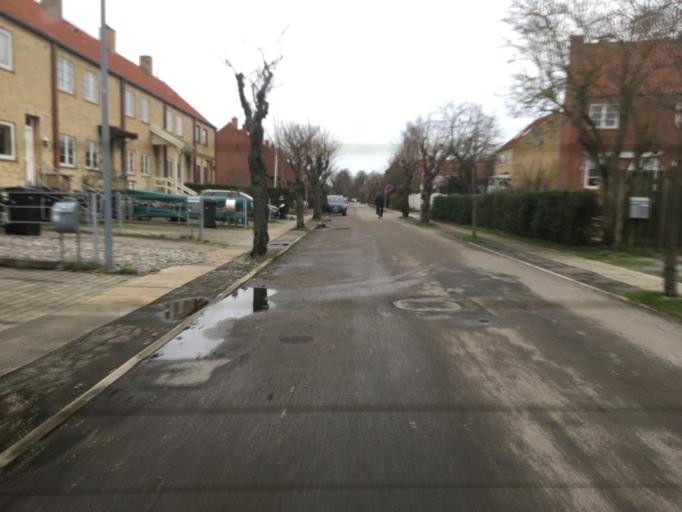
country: DK
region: Capital Region
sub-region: Tarnby Kommune
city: Tarnby
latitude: 55.6210
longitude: 12.6130
